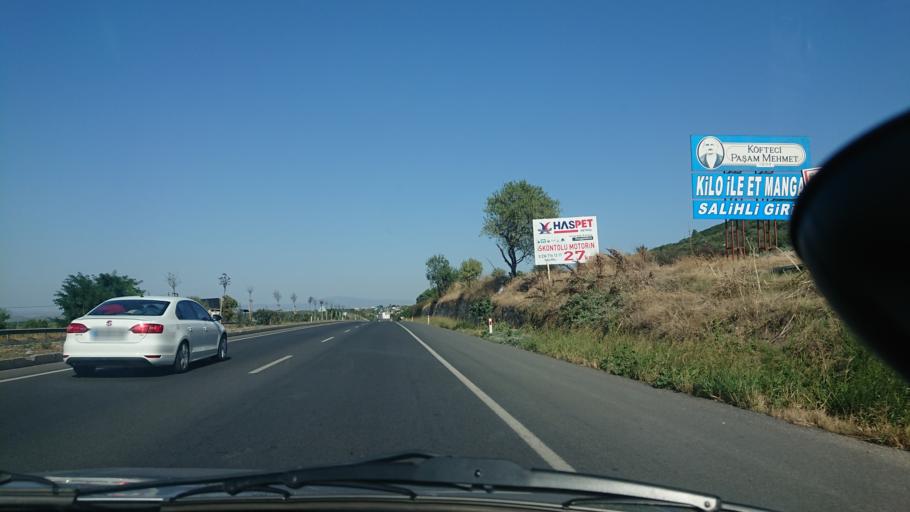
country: TR
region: Manisa
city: Ahmetli
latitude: 38.4915
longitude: 27.8470
